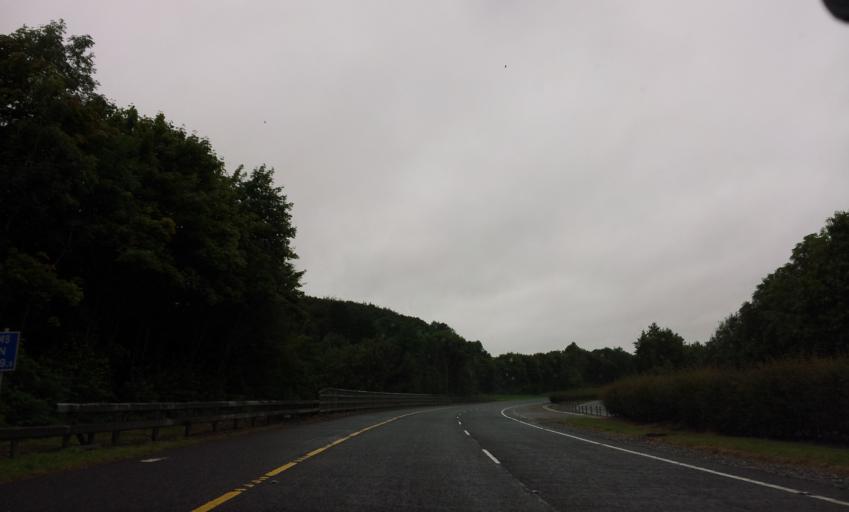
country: IE
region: Munster
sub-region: County Cork
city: Passage West
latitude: 51.9352
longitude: -8.3821
